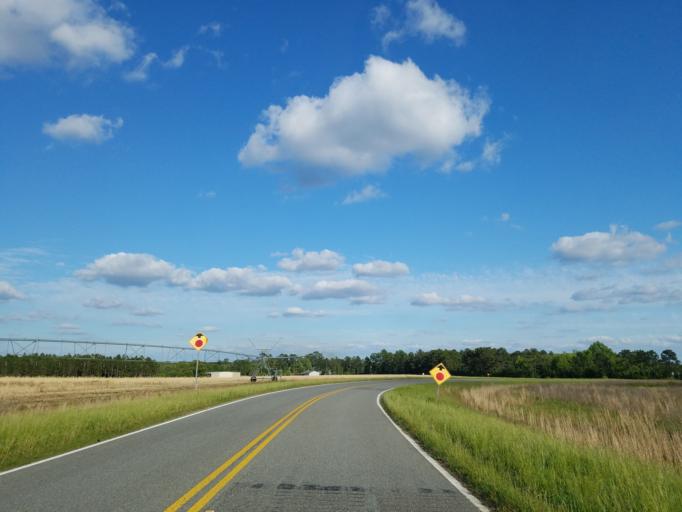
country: US
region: Georgia
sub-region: Turner County
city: Ashburn
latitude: 31.6100
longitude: -83.5637
